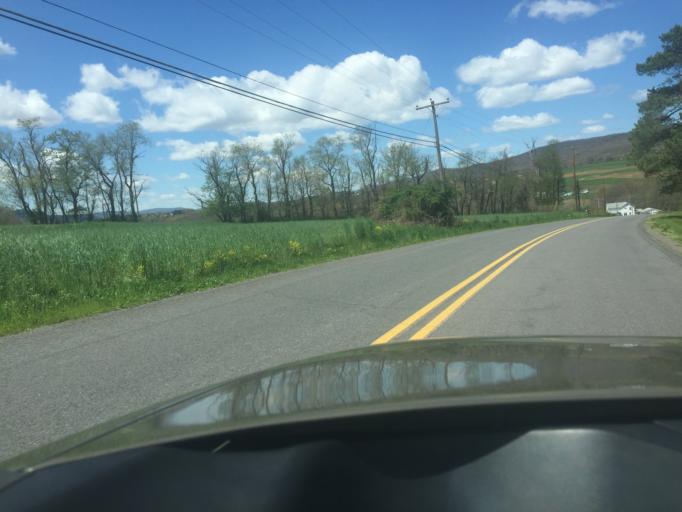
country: US
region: Pennsylvania
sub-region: Luzerne County
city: Conyngham
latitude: 41.0278
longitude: -76.0301
